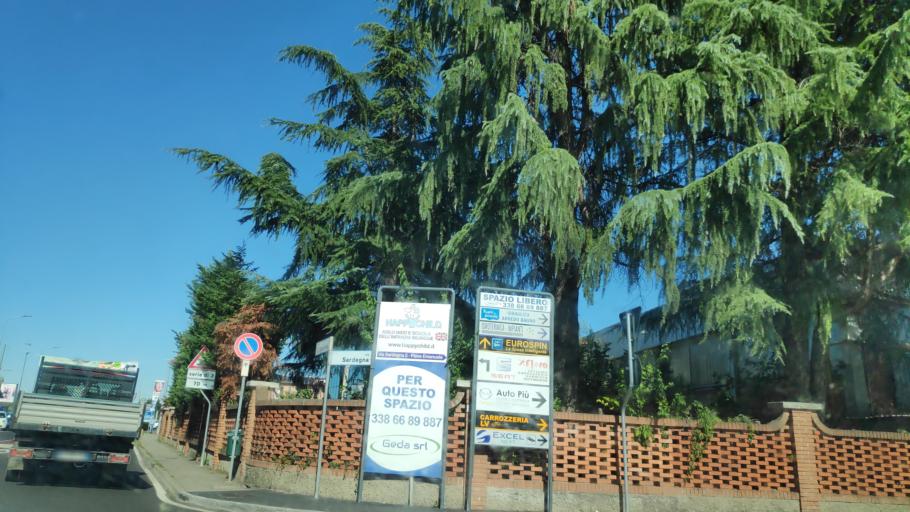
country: IT
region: Lombardy
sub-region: Citta metropolitana di Milano
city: Rozzano
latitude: 45.3747
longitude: 9.1691
